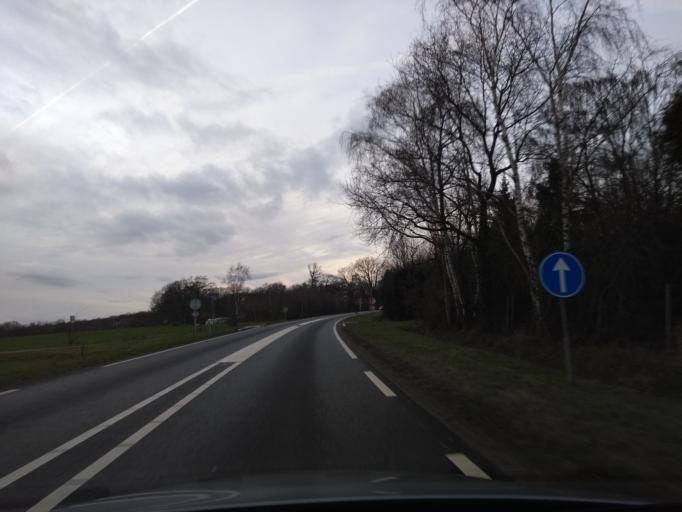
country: NL
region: Overijssel
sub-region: Gemeente Tubbergen
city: Tubbergen
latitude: 52.3662
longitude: 6.8290
